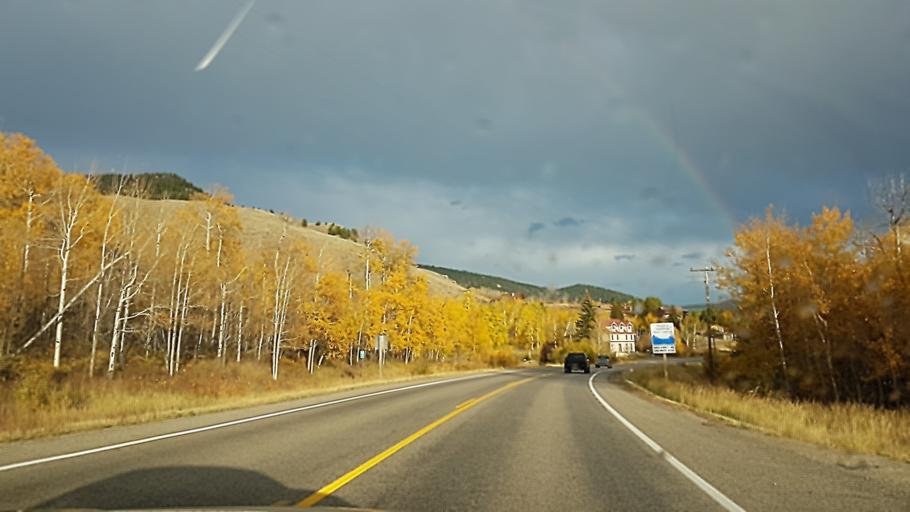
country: US
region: Montana
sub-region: Gallatin County
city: West Yellowstone
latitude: 44.6665
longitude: -111.3895
